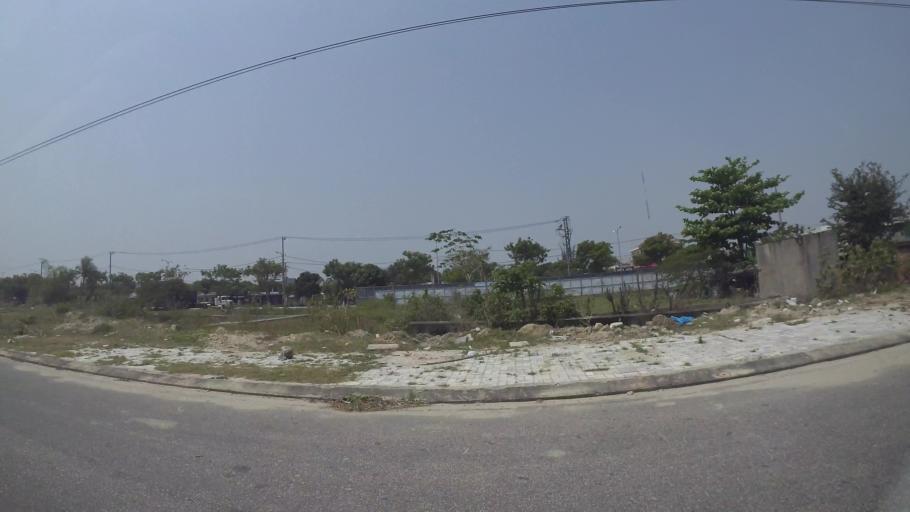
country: VN
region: Da Nang
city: Ngu Hanh Son
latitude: 15.9878
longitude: 108.2580
